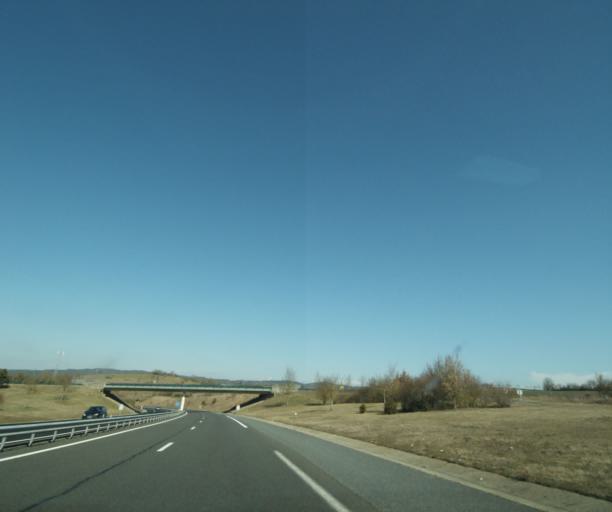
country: FR
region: Midi-Pyrenees
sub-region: Departement de l'Aveyron
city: Severac-le-Chateau
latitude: 44.3069
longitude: 3.1039
